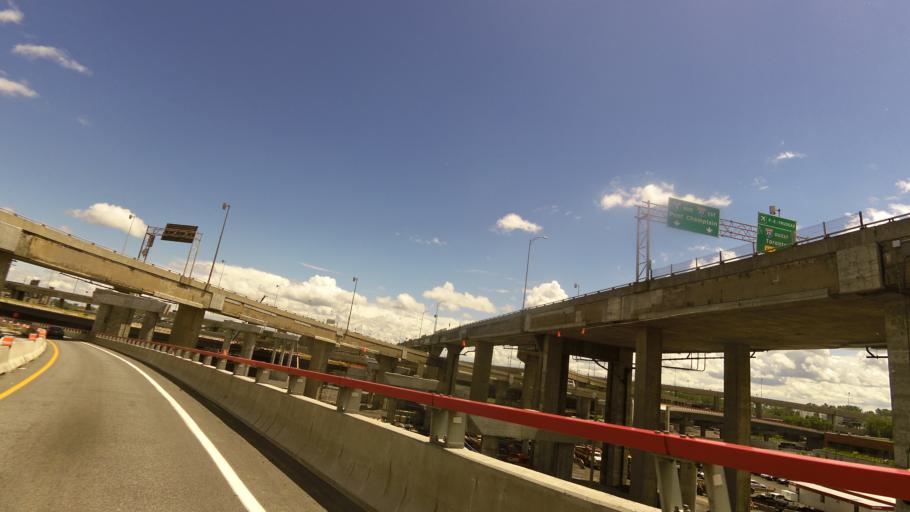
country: CA
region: Quebec
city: Saint-Raymond
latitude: 45.4696
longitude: -73.6025
